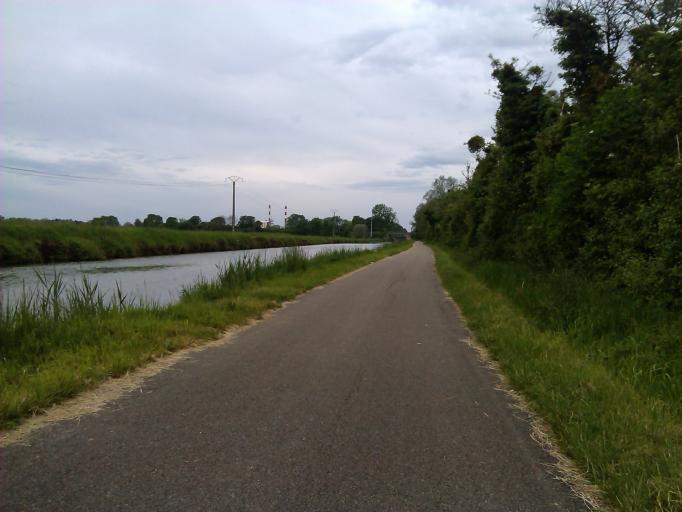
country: FR
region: Franche-Comte
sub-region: Departement du Jura
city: Choisey
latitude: 47.0597
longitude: 5.4355
